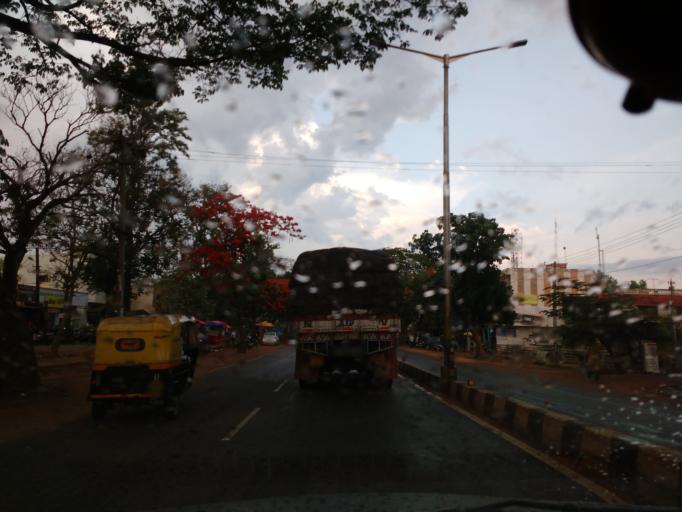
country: IN
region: Karnataka
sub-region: Tumkur
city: Tiptur
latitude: 13.2606
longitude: 76.4693
